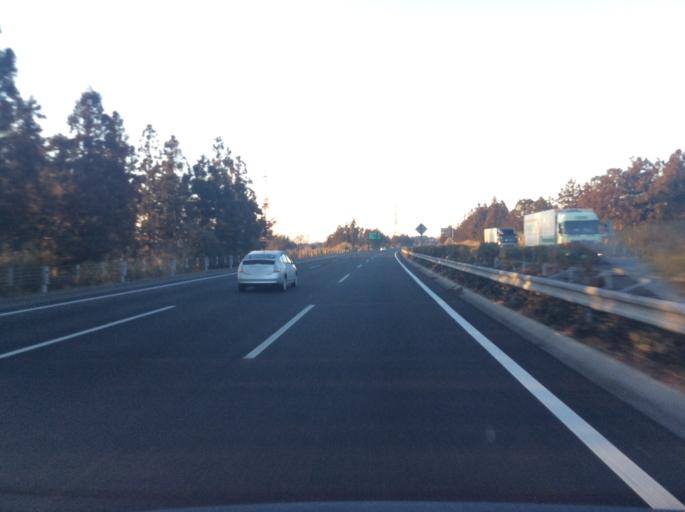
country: JP
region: Ibaraki
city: Mito-shi
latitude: 36.3744
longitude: 140.3846
